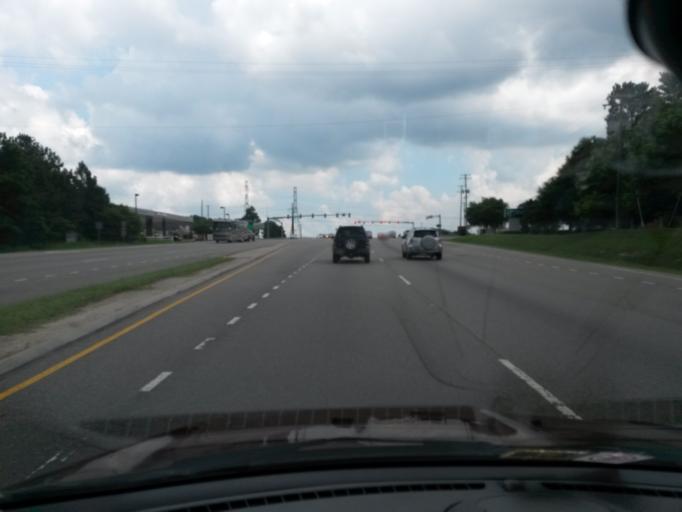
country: US
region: Virginia
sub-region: Chesterfield County
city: Chester
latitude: 37.3542
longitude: -77.3986
